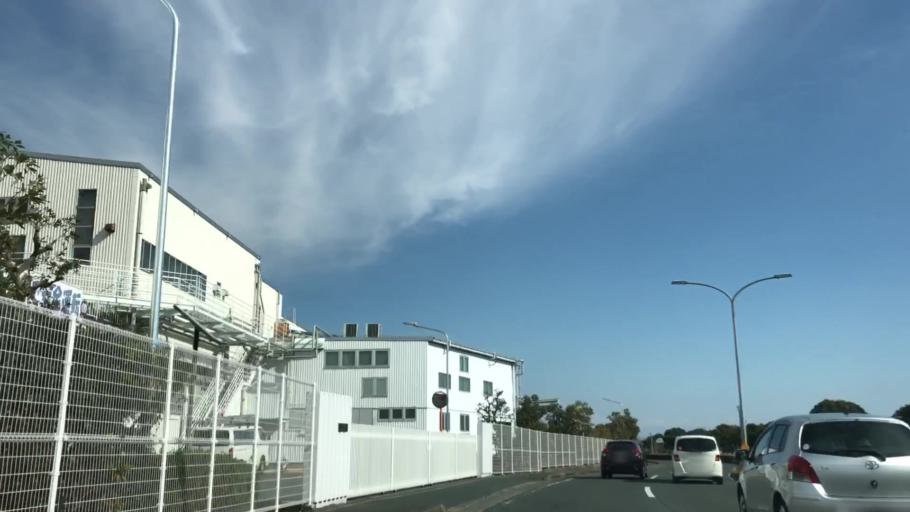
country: JP
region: Shizuoka
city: Hamamatsu
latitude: 34.7526
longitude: 137.7169
